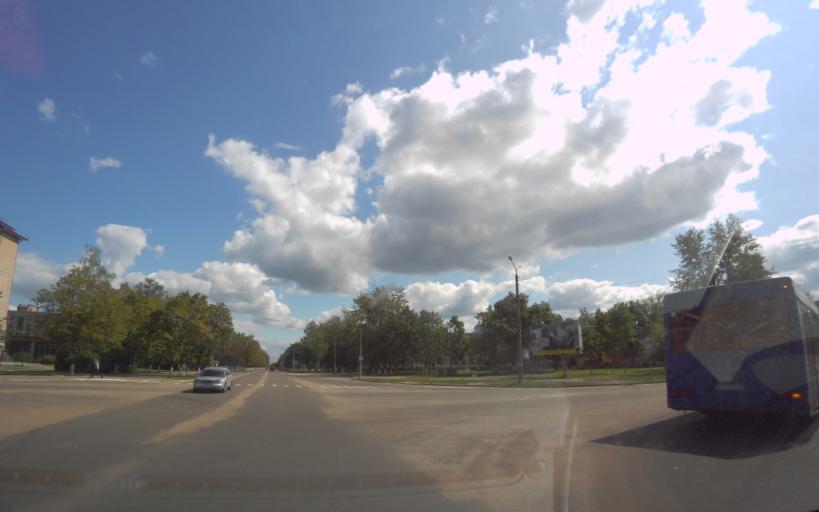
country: BY
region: Minsk
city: Horad Barysaw
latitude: 54.2157
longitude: 28.4785
